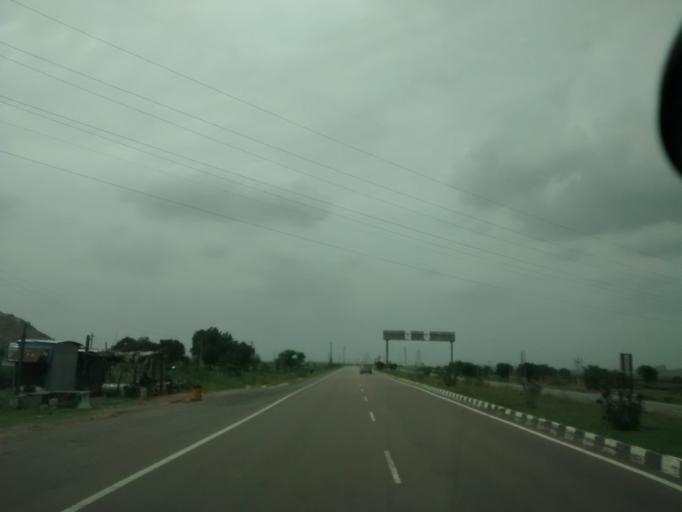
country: IN
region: Andhra Pradesh
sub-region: Kurnool
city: Ramapuram
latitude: 15.1164
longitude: 77.6607
